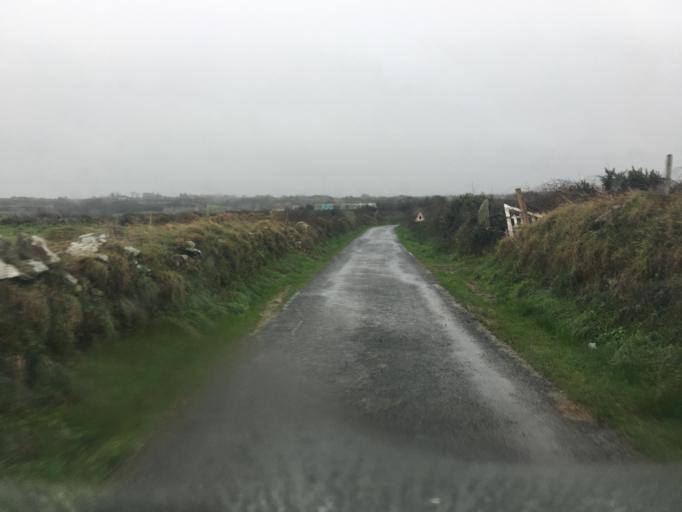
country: FR
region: Lower Normandy
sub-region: Departement de la Manche
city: Beaumont-Hague
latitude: 49.7194
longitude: -1.9203
